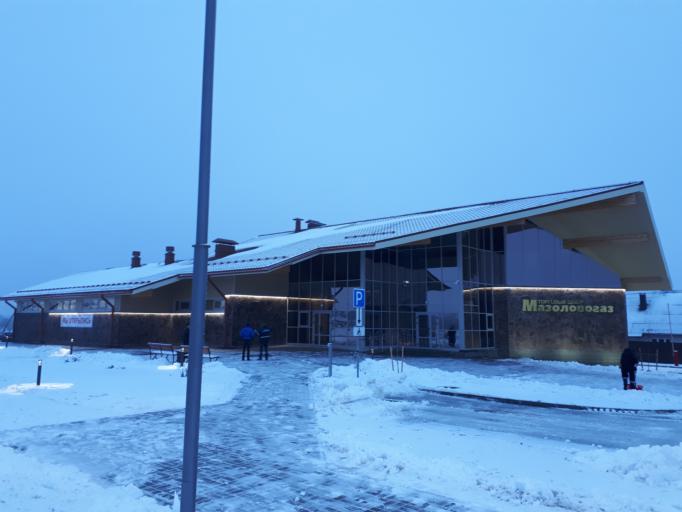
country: BY
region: Vitebsk
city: Vitebsk
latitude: 55.2910
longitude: 30.1411
